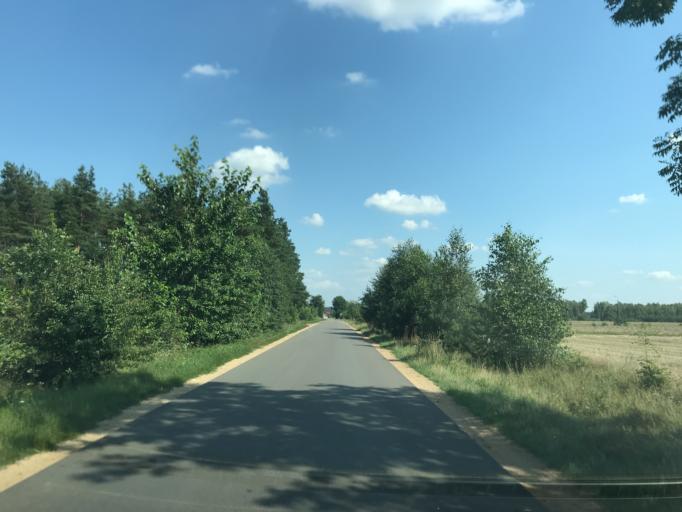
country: PL
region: Masovian Voivodeship
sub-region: Powiat zurominski
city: Lubowidz
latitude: 53.1543
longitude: 19.9239
